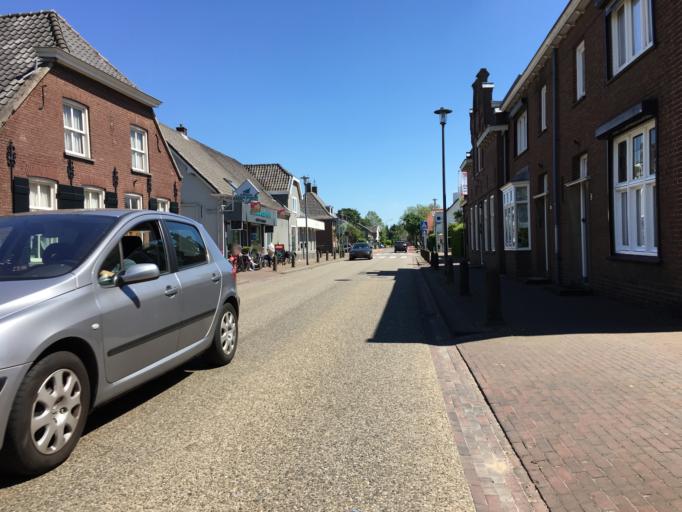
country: NL
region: Gelderland
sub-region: Gemeente Maasdriel
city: Hedel
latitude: 51.7485
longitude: 5.2261
